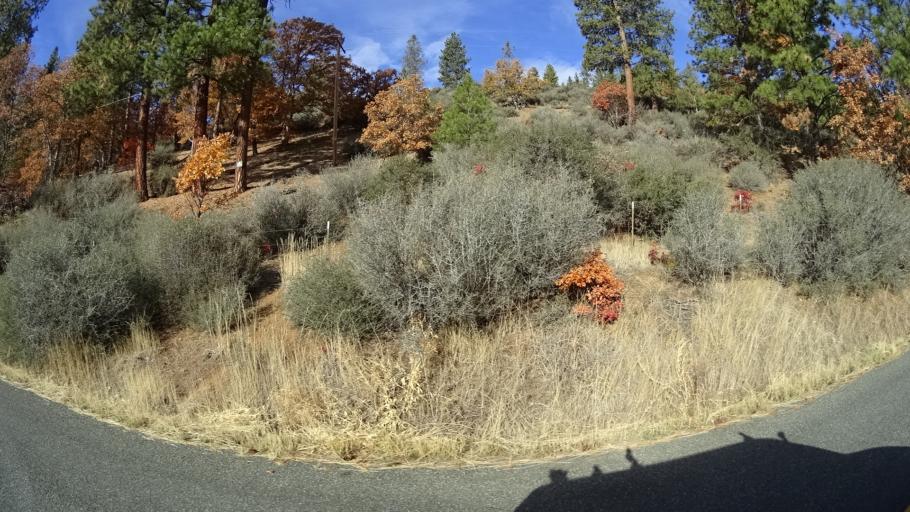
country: US
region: California
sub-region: Siskiyou County
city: Yreka
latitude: 41.6659
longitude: -122.8339
